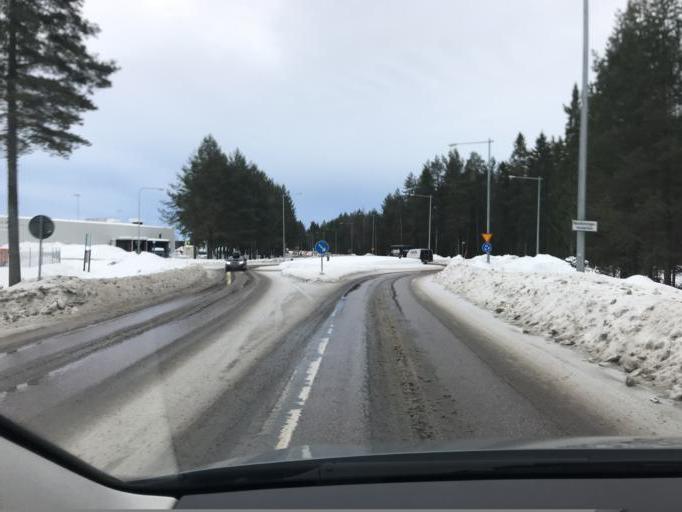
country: SE
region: Norrbotten
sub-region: Lulea Kommun
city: Gammelstad
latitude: 65.6195
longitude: 22.0364
